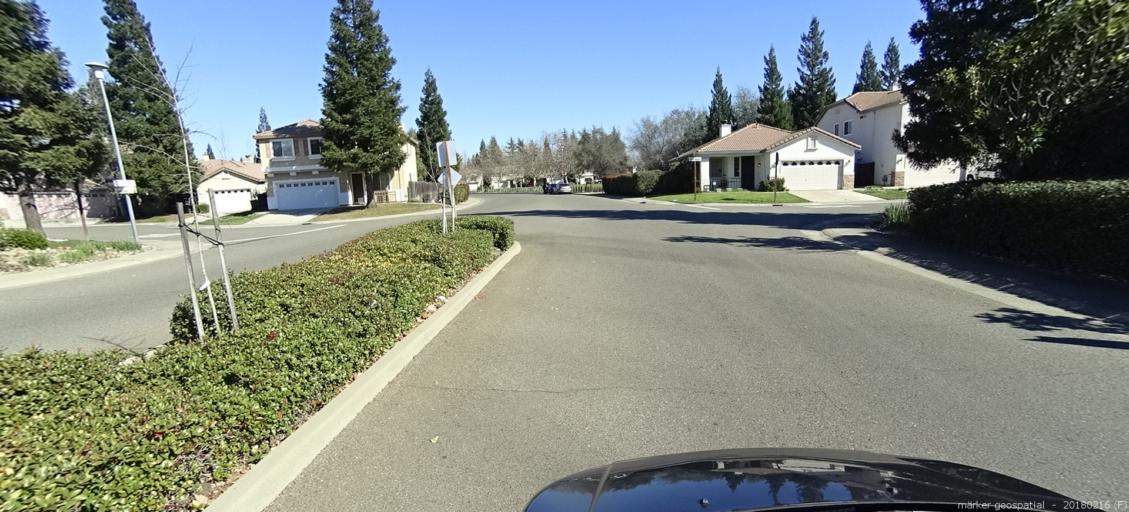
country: US
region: California
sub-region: Sacramento County
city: Gold River
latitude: 38.6175
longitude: -121.2606
